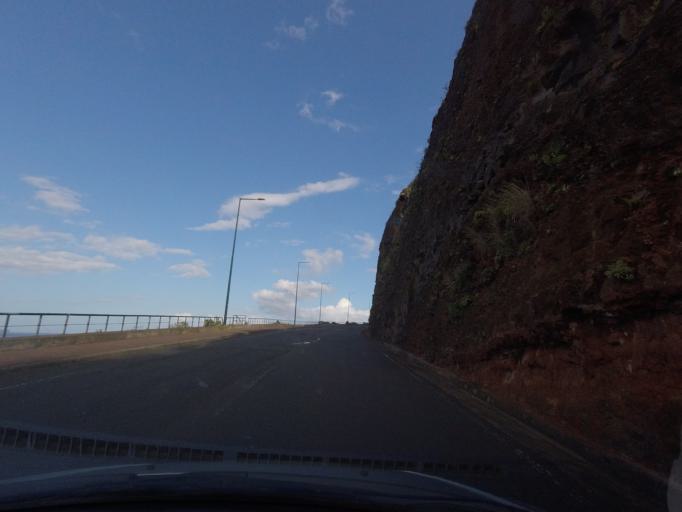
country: PT
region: Madeira
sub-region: Machico
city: Machico
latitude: 32.7133
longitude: -16.7638
